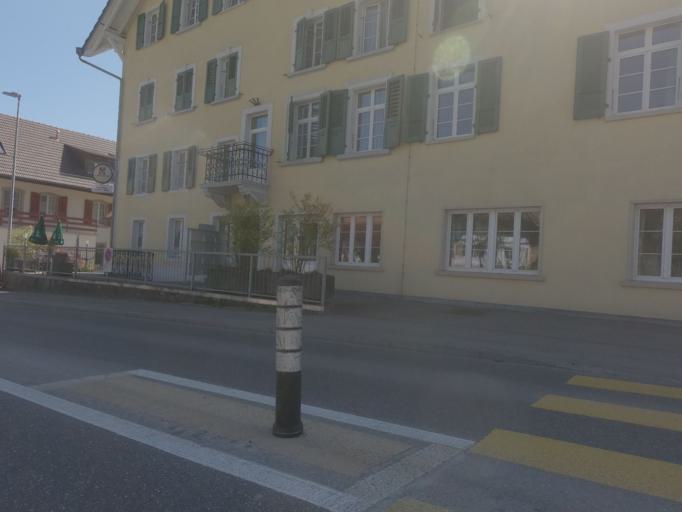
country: CH
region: Bern
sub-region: Biel/Bienne District
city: Orpund
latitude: 47.1204
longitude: 7.3418
